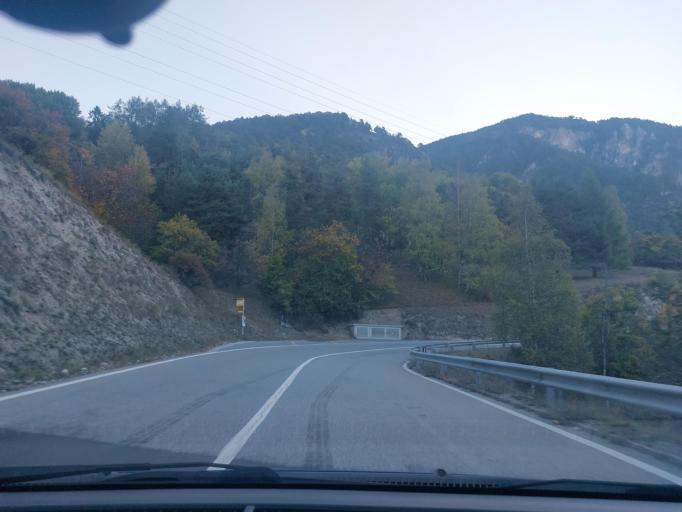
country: CH
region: Valais
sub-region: Sierre District
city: Chippis
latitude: 46.2600
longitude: 7.5649
